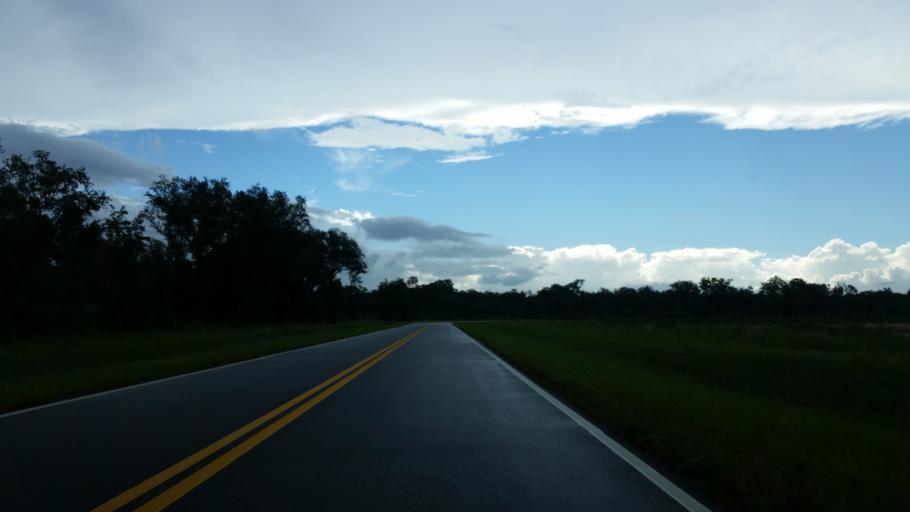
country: US
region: Florida
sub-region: Walton County
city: DeFuniak Springs
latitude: 30.7390
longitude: -86.3319
